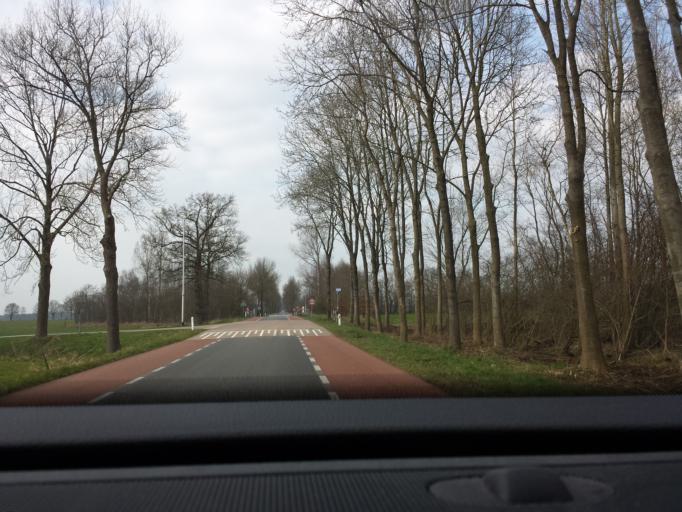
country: NL
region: Gelderland
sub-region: Berkelland
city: Borculo
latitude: 52.0418
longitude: 6.4805
